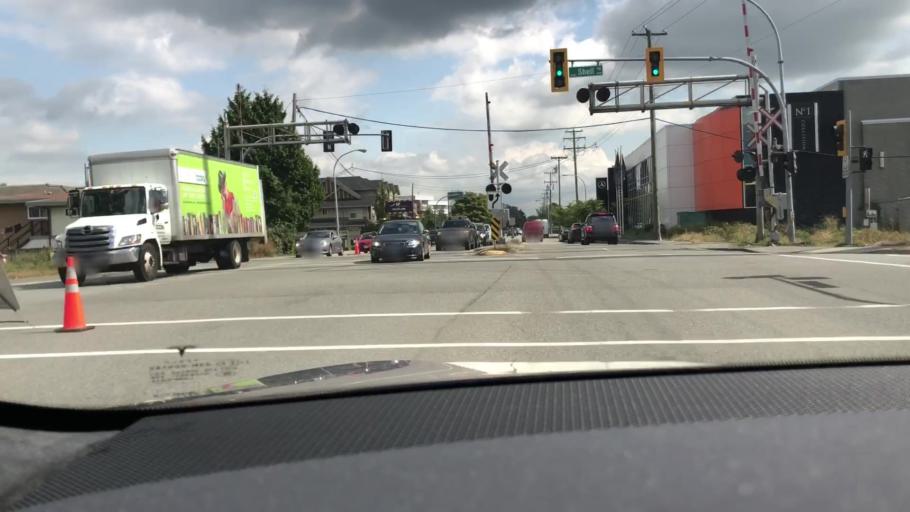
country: CA
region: British Columbia
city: Richmond
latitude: 49.1845
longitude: -123.1029
